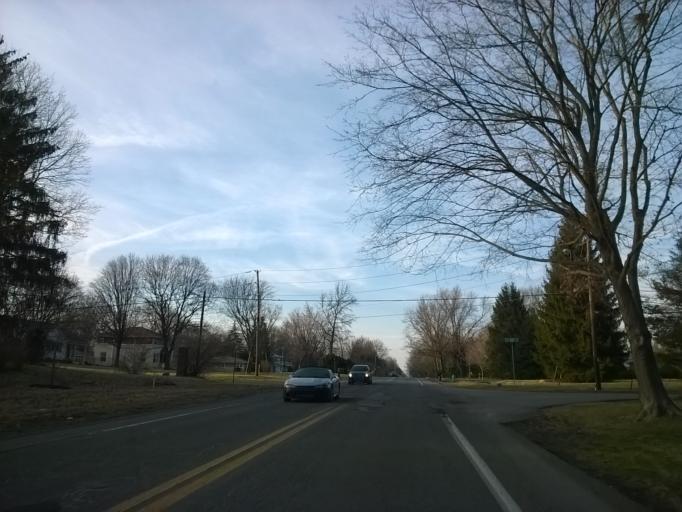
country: US
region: Indiana
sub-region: Marion County
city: Speedway
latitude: 39.8414
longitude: -86.2118
